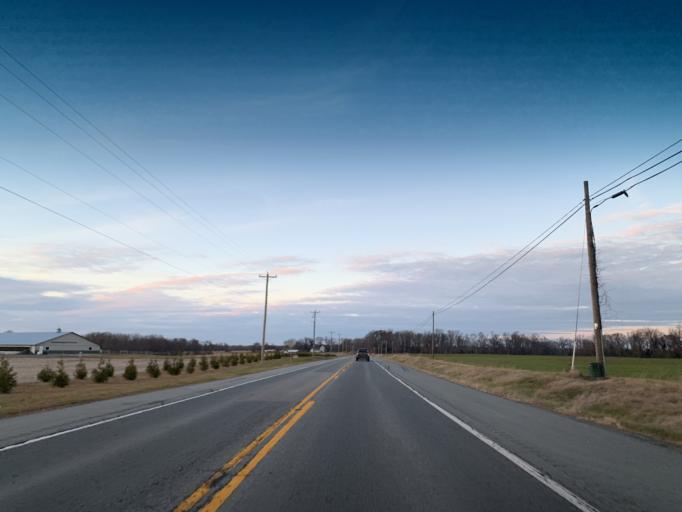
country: US
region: Delaware
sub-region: New Castle County
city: Middletown
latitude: 39.4473
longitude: -75.8690
